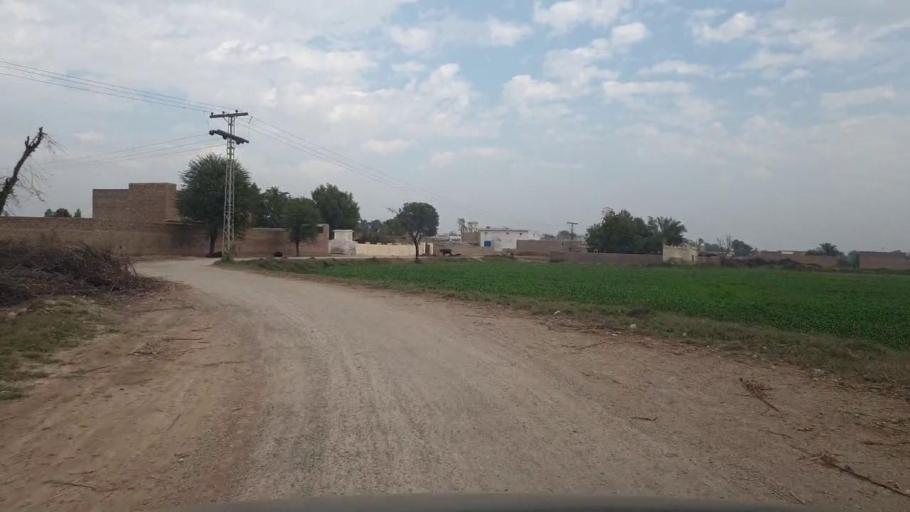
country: PK
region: Sindh
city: Sakrand
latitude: 26.0313
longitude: 68.4088
